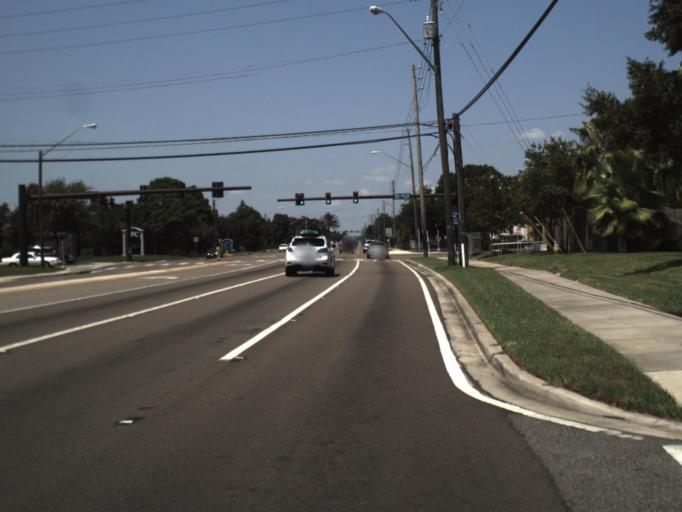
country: US
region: Florida
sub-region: Pinellas County
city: South Pasadena
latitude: 27.7764
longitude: -82.7283
